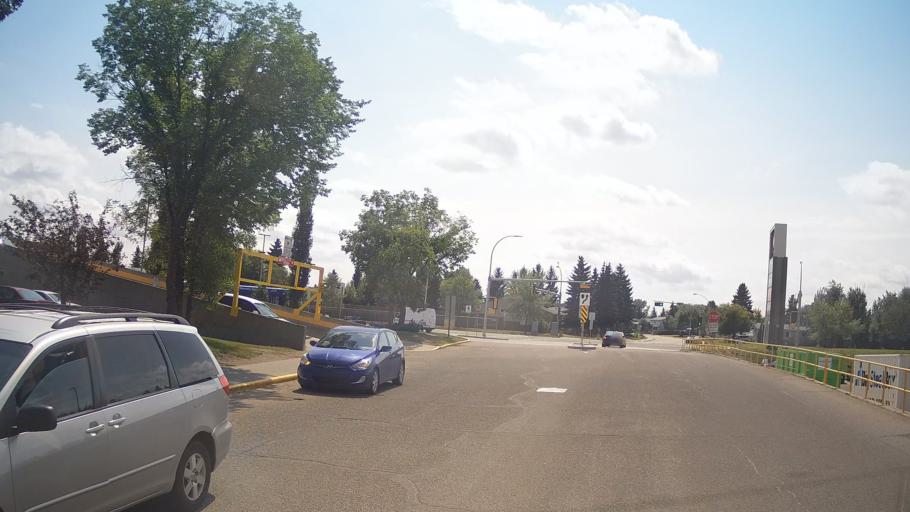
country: CA
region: Alberta
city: St. Albert
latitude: 53.5212
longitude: -113.6235
